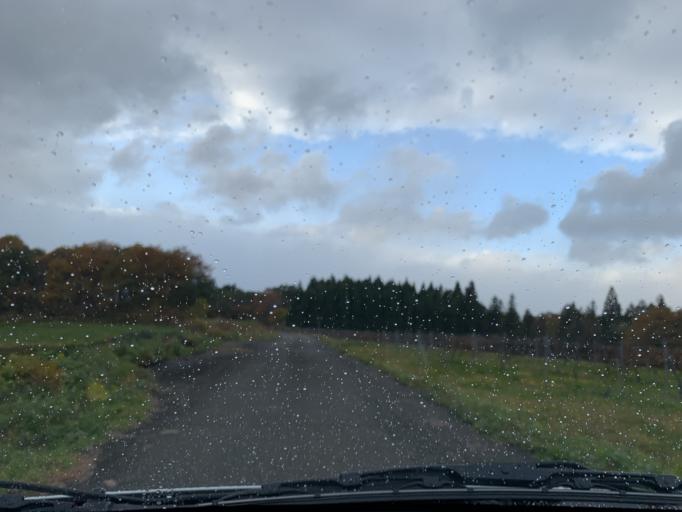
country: JP
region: Iwate
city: Mizusawa
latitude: 39.0877
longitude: 141.0045
